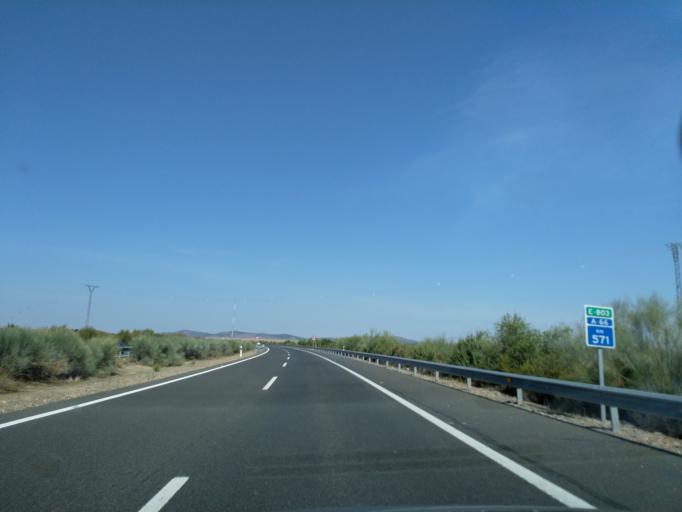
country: ES
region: Extremadura
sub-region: Provincia de Caceres
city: Aldea del Cano
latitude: 39.3297
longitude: -6.3313
